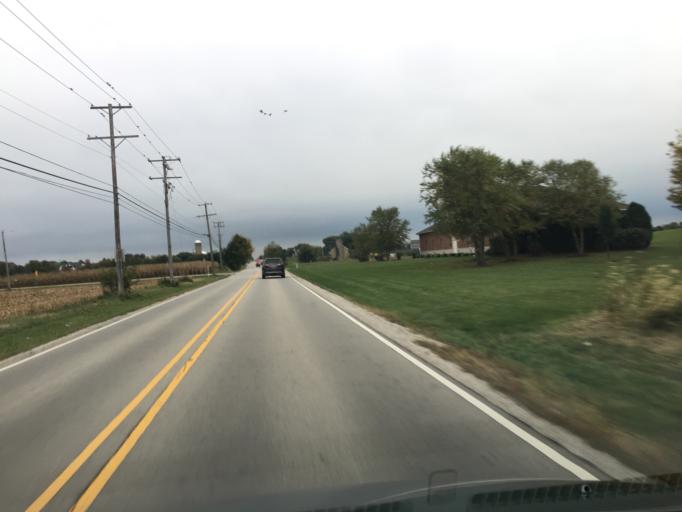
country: US
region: Illinois
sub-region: Will County
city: Plainfield
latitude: 41.6519
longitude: -88.1857
